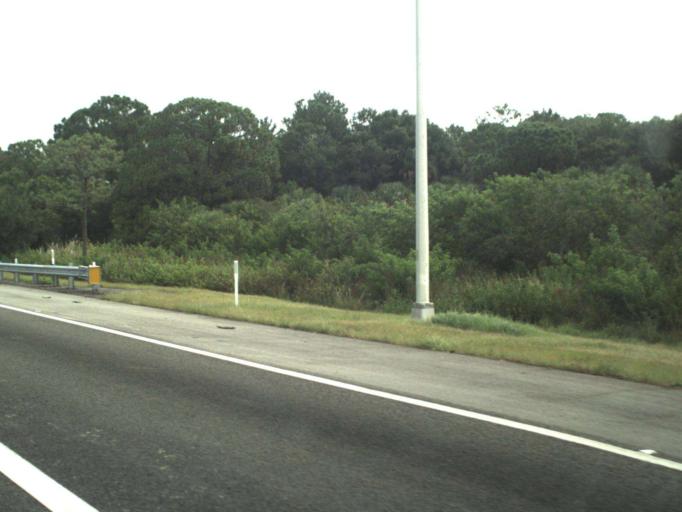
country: US
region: Florida
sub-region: Saint Lucie County
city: Fort Pierce South
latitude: 27.4091
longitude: -80.3882
